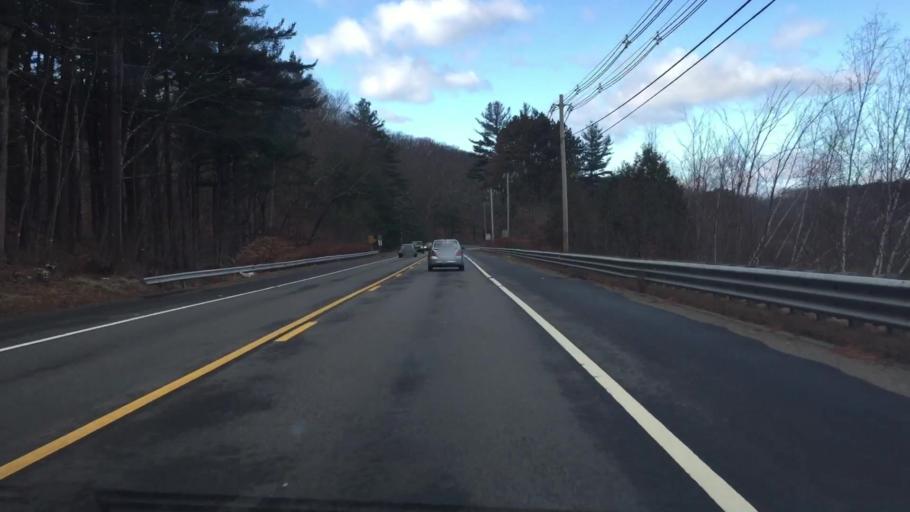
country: US
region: Massachusetts
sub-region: Worcester County
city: West Boylston
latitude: 42.3436
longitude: -71.7602
